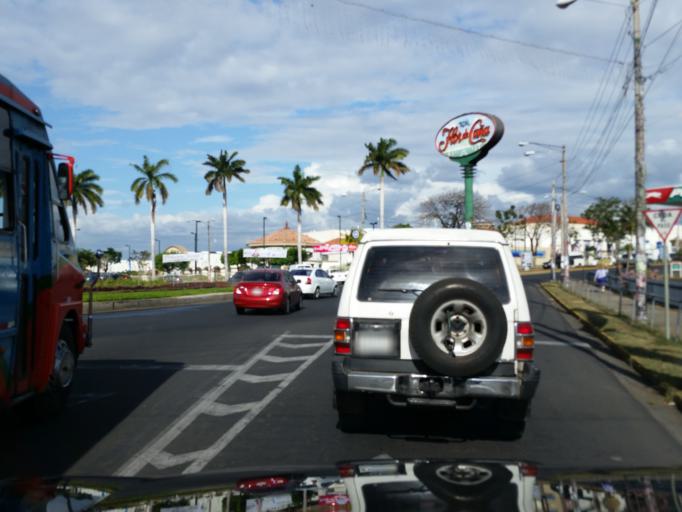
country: NI
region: Managua
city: Managua
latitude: 12.1288
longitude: -86.2669
